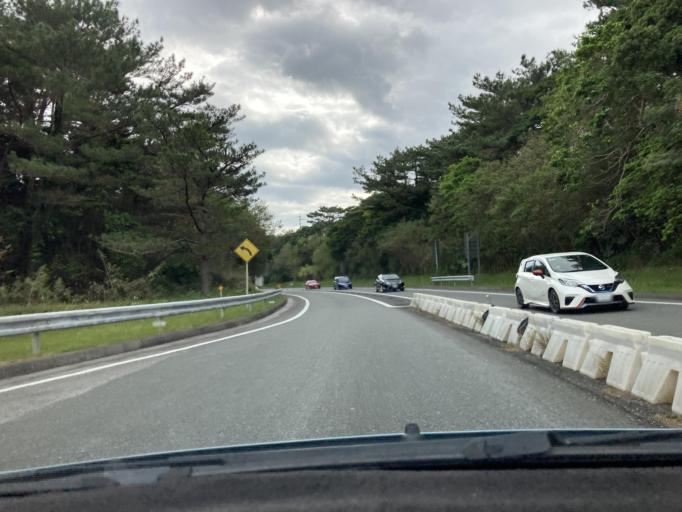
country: JP
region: Okinawa
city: Nago
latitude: 26.4871
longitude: 127.9691
